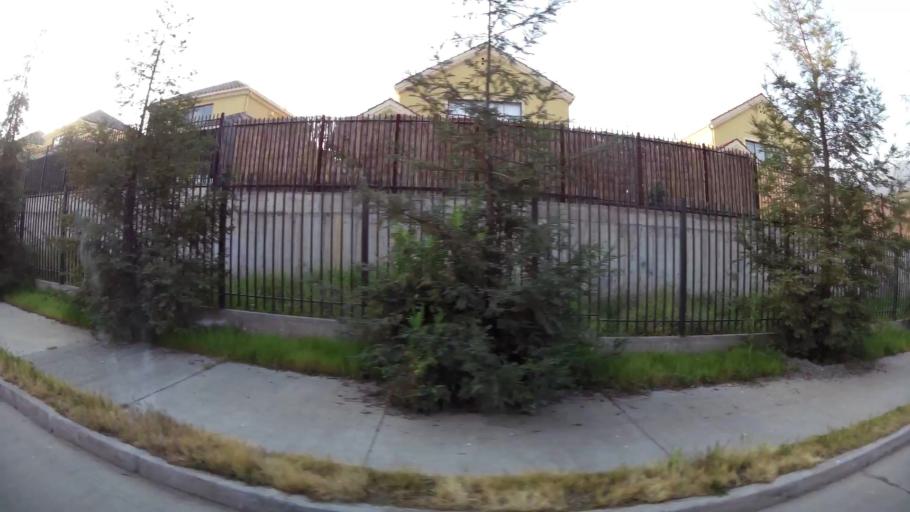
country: CL
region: Santiago Metropolitan
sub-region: Provincia de Santiago
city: Villa Presidente Frei, Nunoa, Santiago, Chile
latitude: -33.3306
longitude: -70.5022
